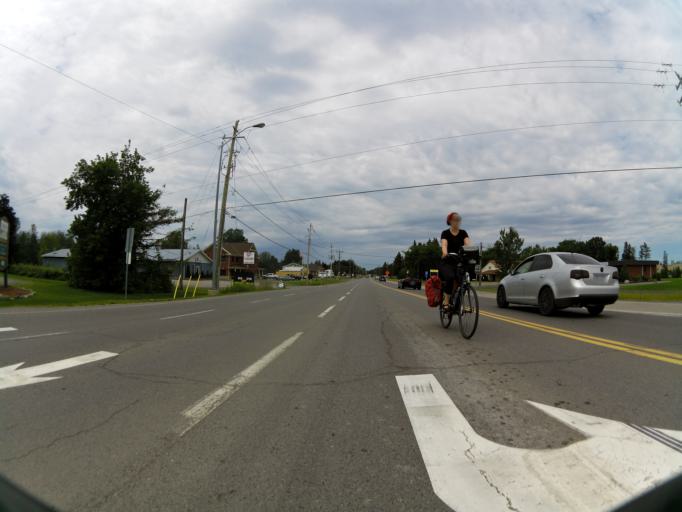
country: CA
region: Ontario
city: Prescott
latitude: 45.0217
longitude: -75.6533
